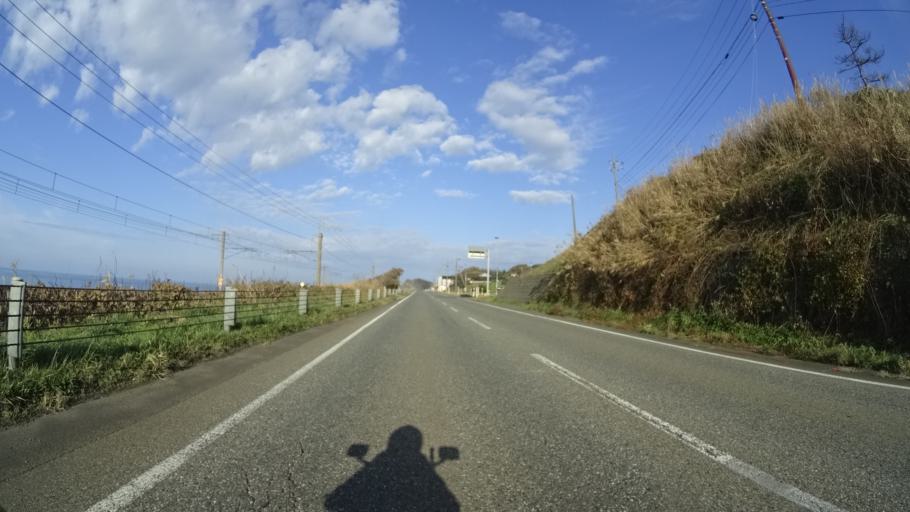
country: JP
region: Niigata
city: Kashiwazaki
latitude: 37.3067
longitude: 138.4194
